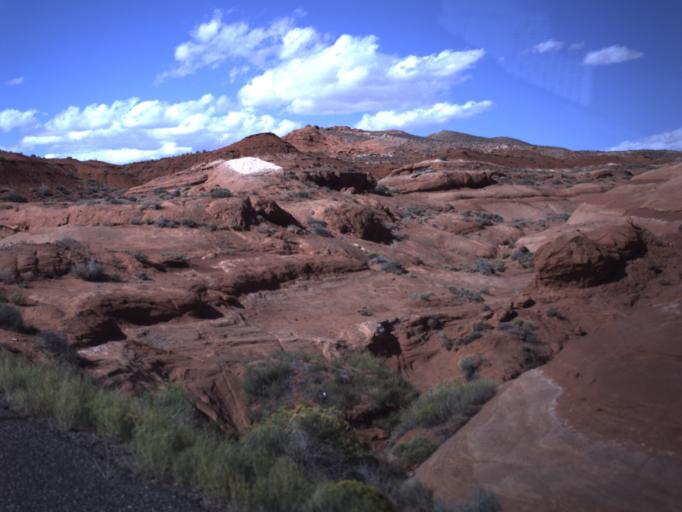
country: US
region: Utah
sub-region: Wayne County
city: Loa
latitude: 38.0620
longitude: -110.5981
